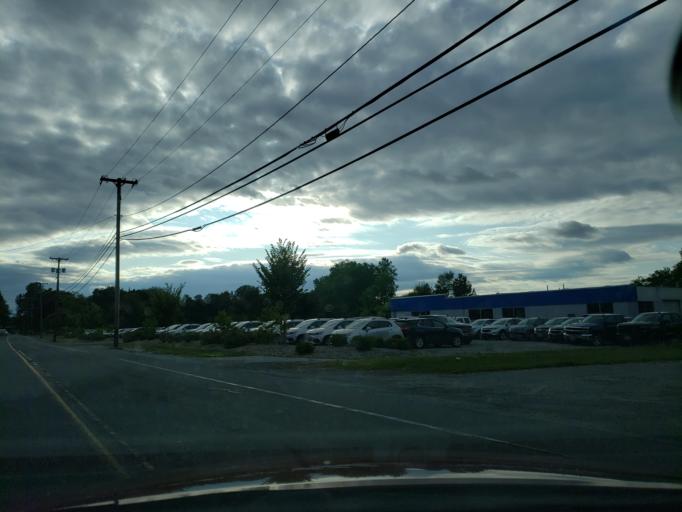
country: US
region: New York
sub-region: Monroe County
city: Greece
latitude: 43.2175
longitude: -77.6539
